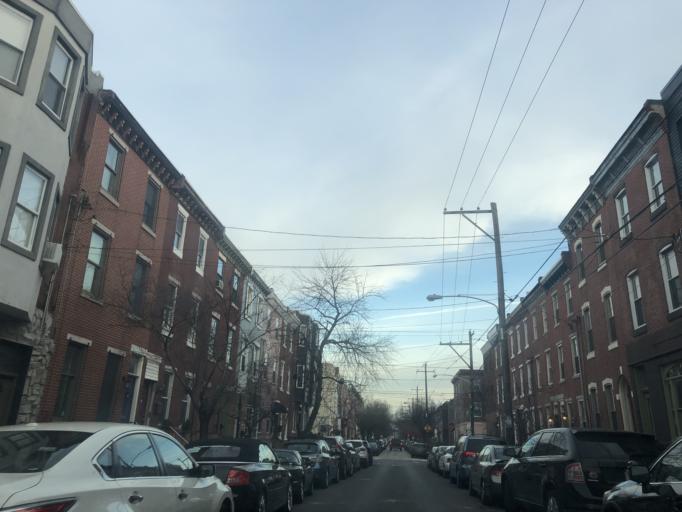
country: US
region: Pennsylvania
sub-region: Philadelphia County
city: Philadelphia
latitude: 39.9362
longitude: -75.1640
